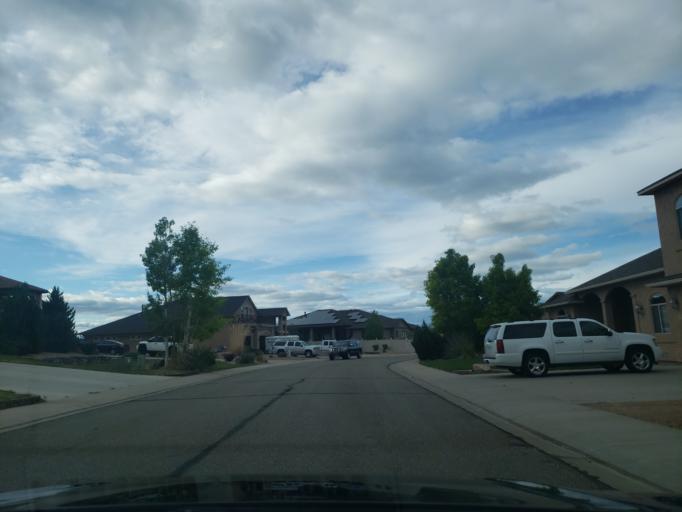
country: US
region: Colorado
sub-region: Mesa County
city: Redlands
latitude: 39.1080
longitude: -108.6694
